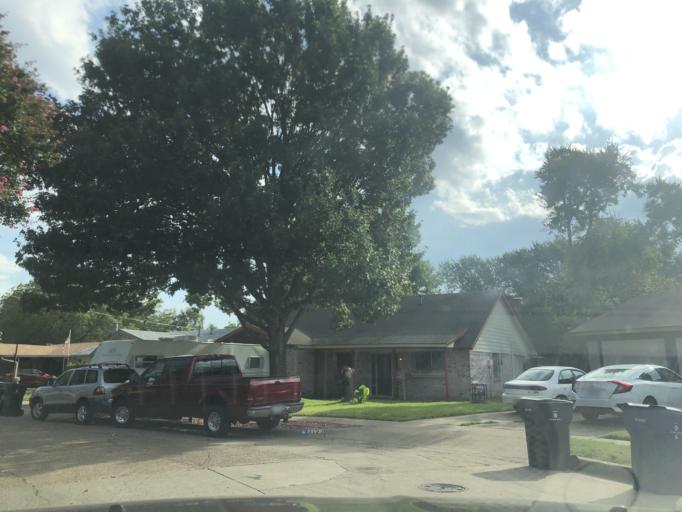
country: US
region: Texas
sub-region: Dallas County
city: Garland
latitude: 32.8850
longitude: -96.6587
